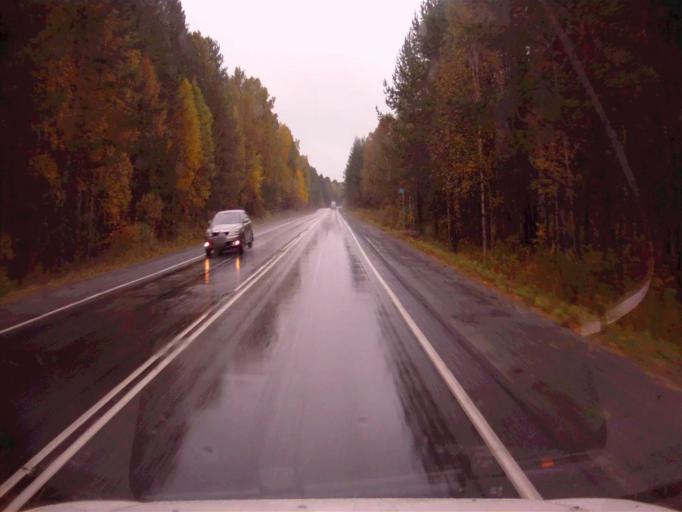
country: RU
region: Chelyabinsk
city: Tayginka
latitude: 55.5528
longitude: 60.6463
